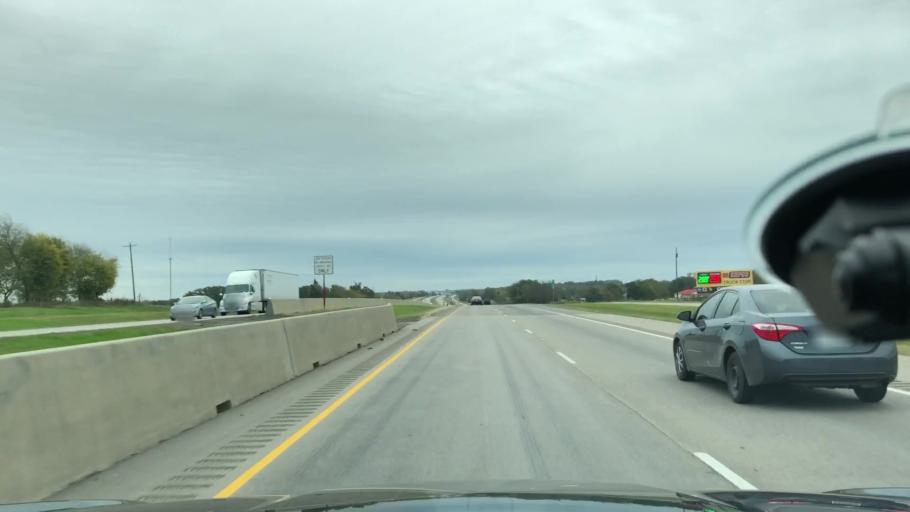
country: US
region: Texas
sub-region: Franklin County
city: Mount Vernon
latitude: 33.1638
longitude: -95.2668
